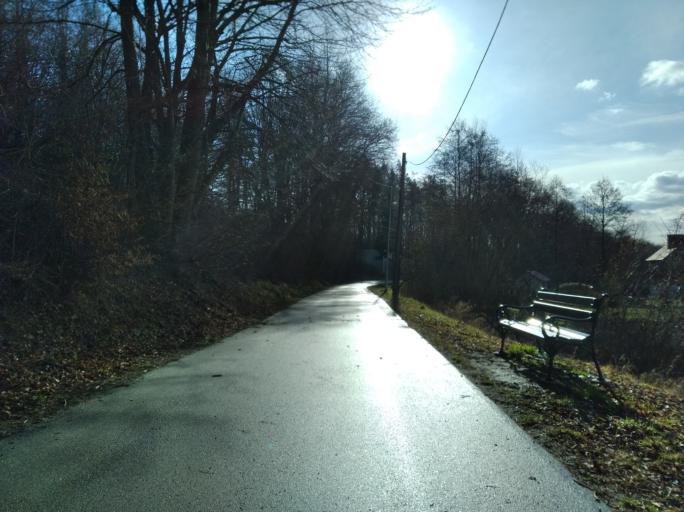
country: PL
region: Subcarpathian Voivodeship
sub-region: Powiat strzyzowski
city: Strzyzow
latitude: 49.8757
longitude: 21.7784
